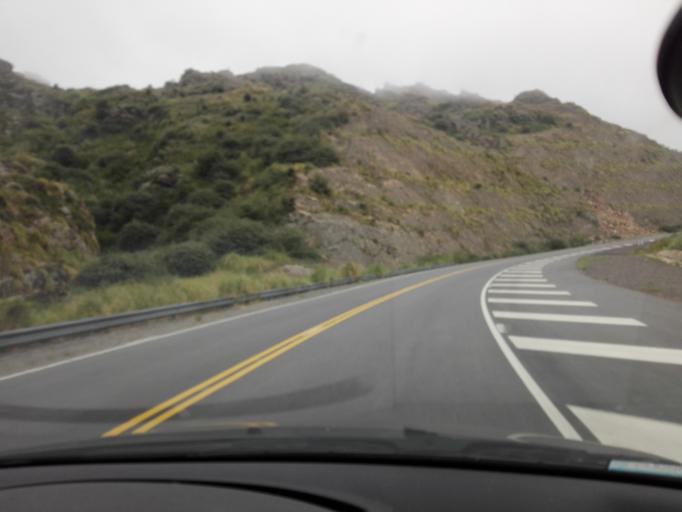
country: AR
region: Cordoba
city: Cuesta Blanca
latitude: -31.6148
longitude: -64.6919
